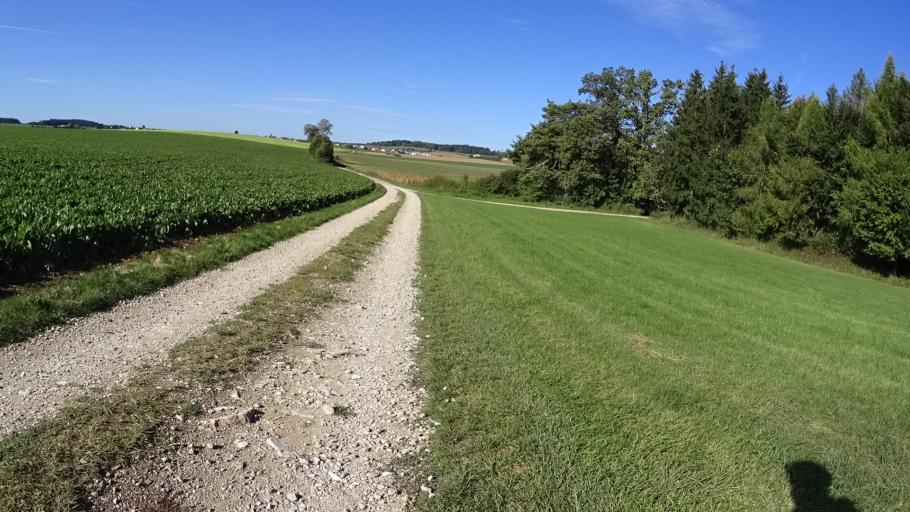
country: DE
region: Bavaria
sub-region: Upper Bavaria
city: Adelschlag
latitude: 48.8631
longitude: 11.2628
